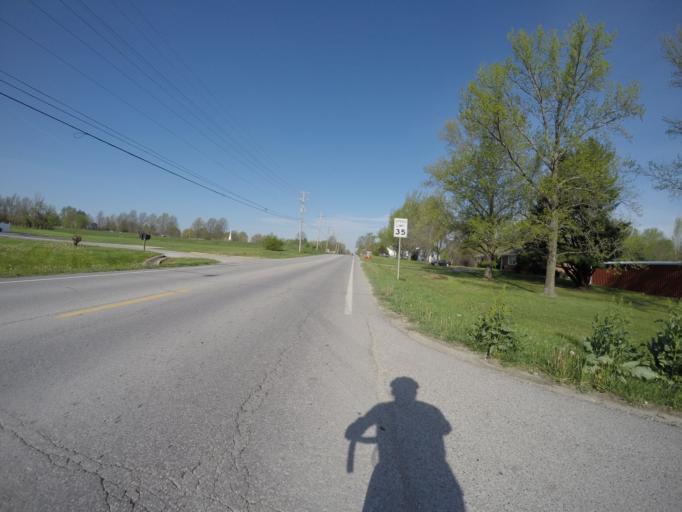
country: US
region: Missouri
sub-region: Jackson County
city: Greenwood
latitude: 38.8517
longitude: -94.3499
